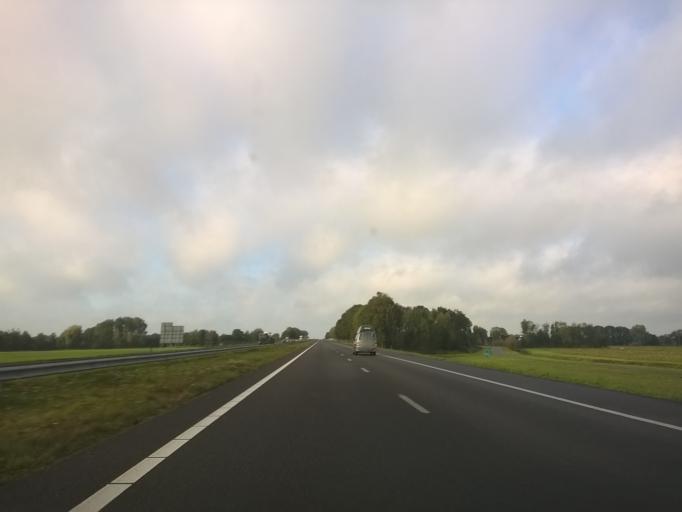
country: NL
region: Groningen
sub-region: Gemeente Grootegast
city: Grootegast
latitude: 53.1484
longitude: 6.2507
